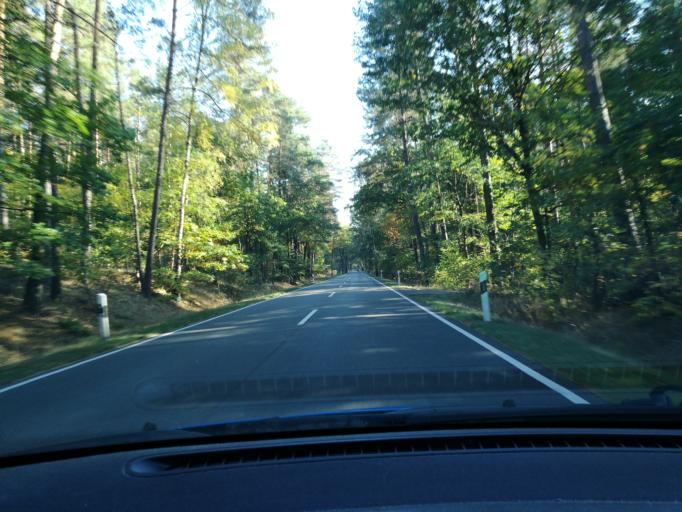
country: DE
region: Lower Saxony
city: Karwitz
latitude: 53.1220
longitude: 10.9845
